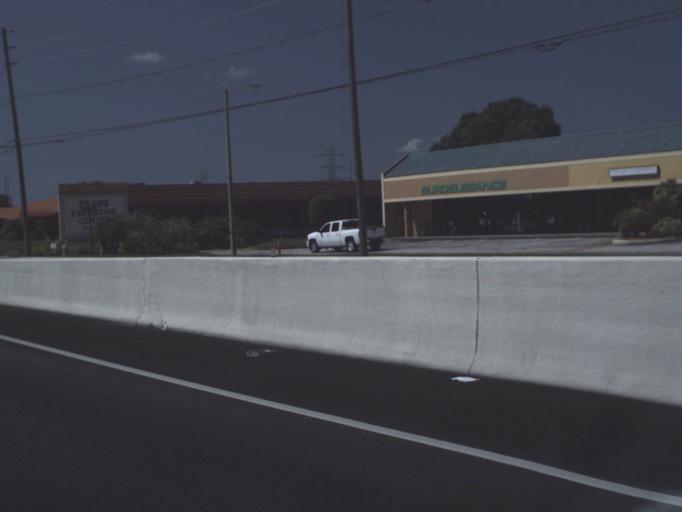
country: US
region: Florida
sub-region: Pinellas County
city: Safety Harbor
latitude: 28.0061
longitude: -82.7298
